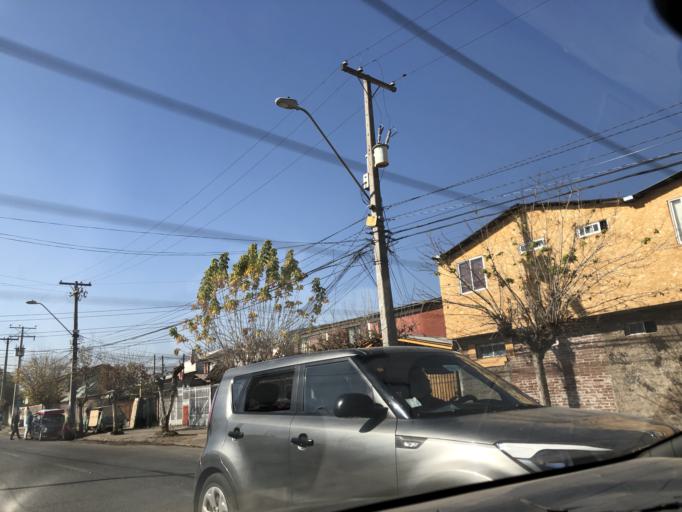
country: CL
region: Santiago Metropolitan
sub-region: Provincia de Santiago
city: La Pintana
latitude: -33.5837
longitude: -70.5985
